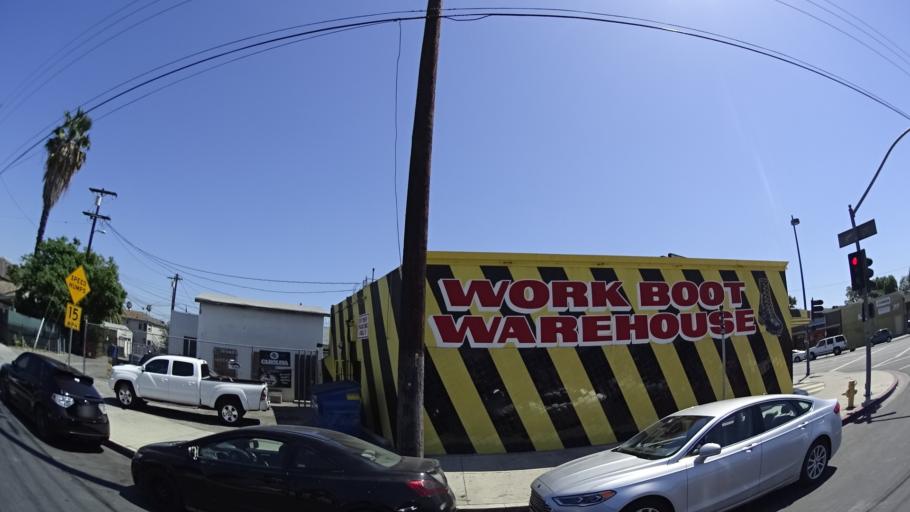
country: US
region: California
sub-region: Los Angeles County
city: North Hollywood
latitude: 34.1757
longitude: -118.3808
